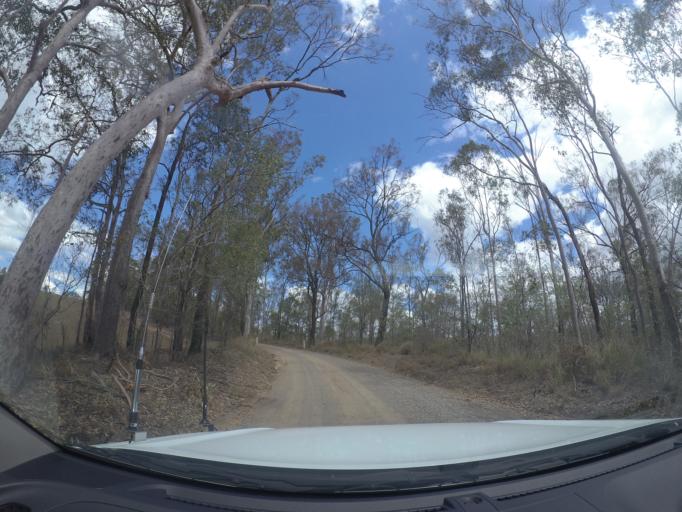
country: AU
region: Queensland
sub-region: Logan
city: Cedar Vale
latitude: -27.8909
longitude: 153.0439
